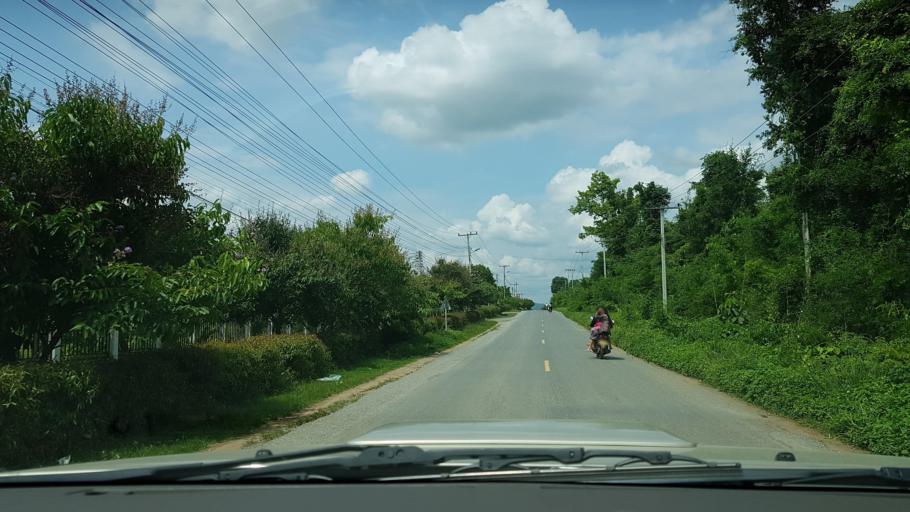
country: LA
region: Loungnamtha
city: Muang Nale
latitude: 20.1279
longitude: 101.4397
